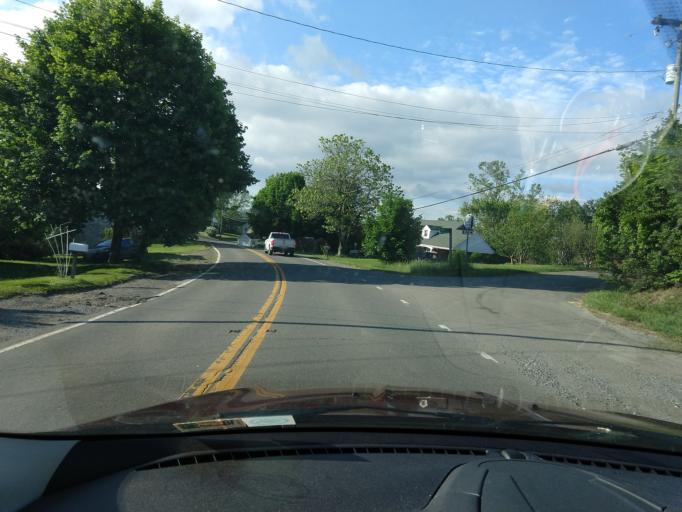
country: US
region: Virginia
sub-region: City of Galax
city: Galax
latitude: 36.7307
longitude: -80.9816
